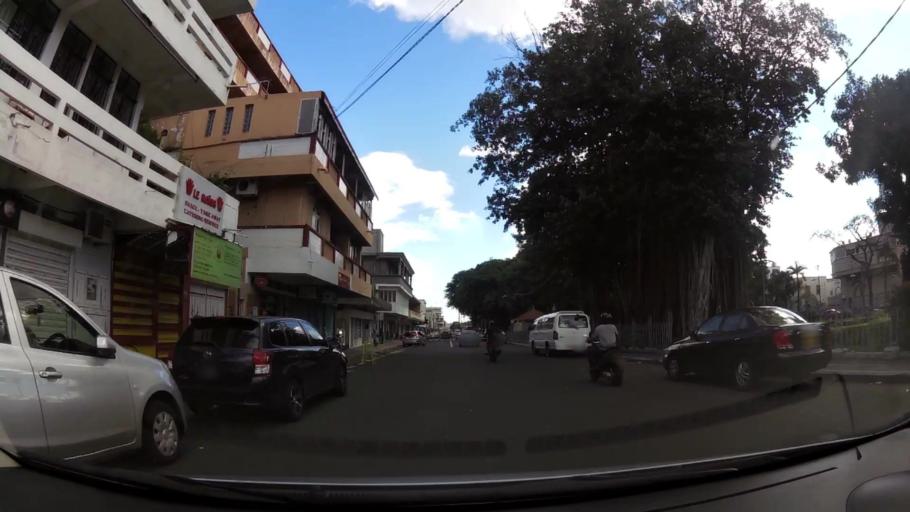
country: MU
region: Port Louis
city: Port Louis
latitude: -20.1605
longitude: 57.5127
